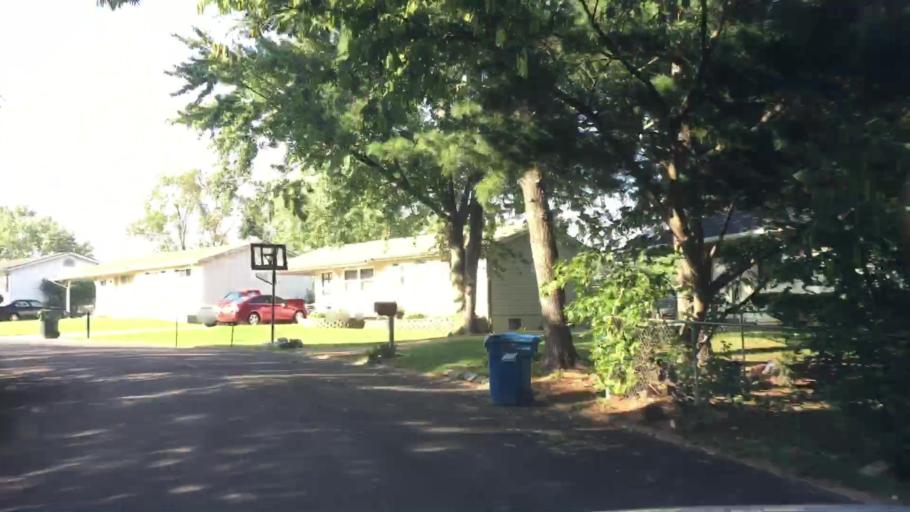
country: US
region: Missouri
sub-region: Jefferson County
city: Arnold
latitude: 38.4462
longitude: -90.3580
